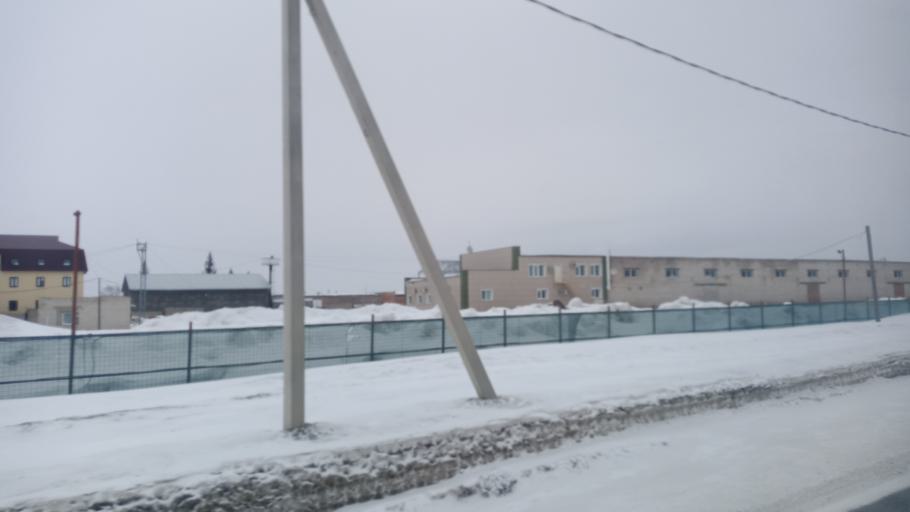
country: RU
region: Altai Krai
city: Novosilikatnyy
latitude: 53.3902
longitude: 83.6709
